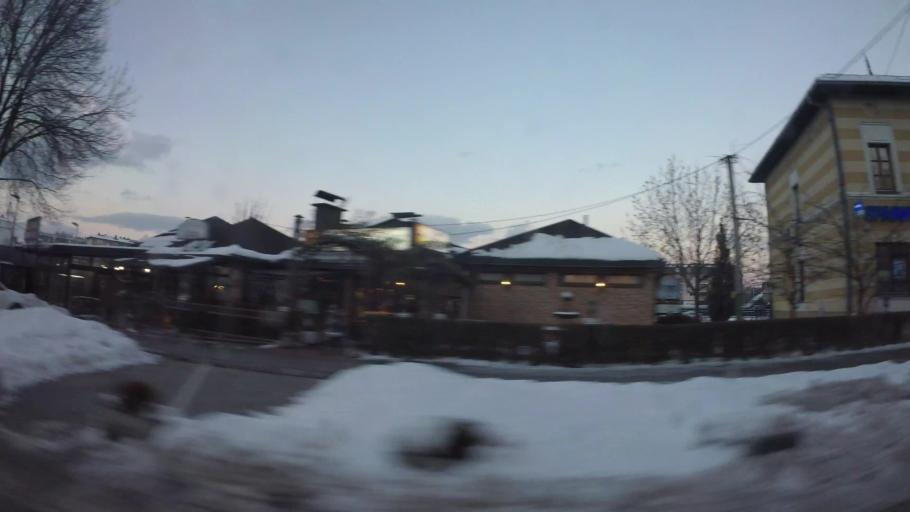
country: BA
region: Federation of Bosnia and Herzegovina
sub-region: Kanton Sarajevo
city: Sarajevo
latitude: 43.8299
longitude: 18.3036
